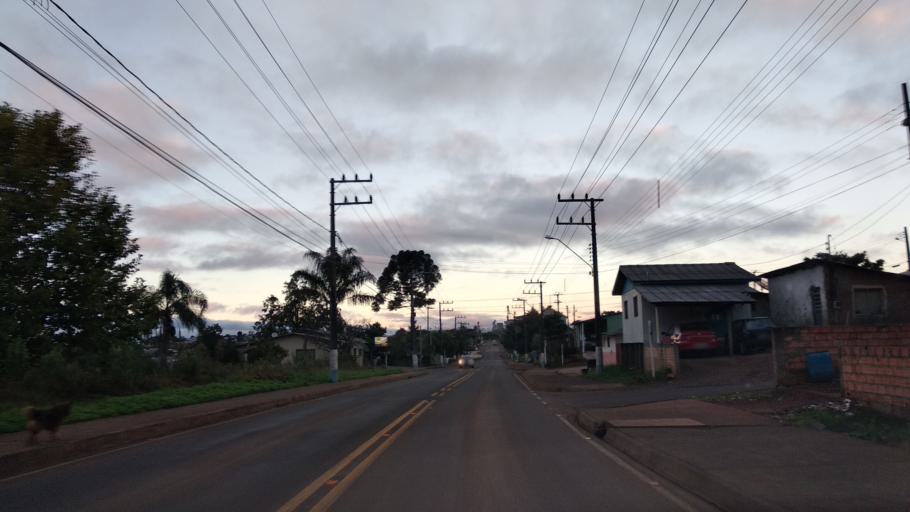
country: BR
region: Santa Catarina
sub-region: Campos Novos
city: Campos Novos
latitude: -27.3831
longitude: -51.2104
